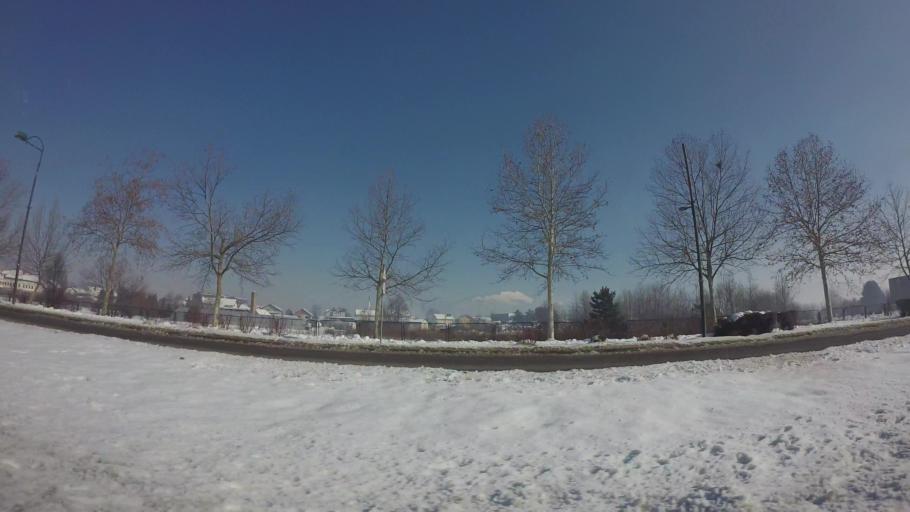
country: BA
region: Federation of Bosnia and Herzegovina
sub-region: Kanton Sarajevo
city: Sarajevo
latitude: 43.8092
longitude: 18.3104
